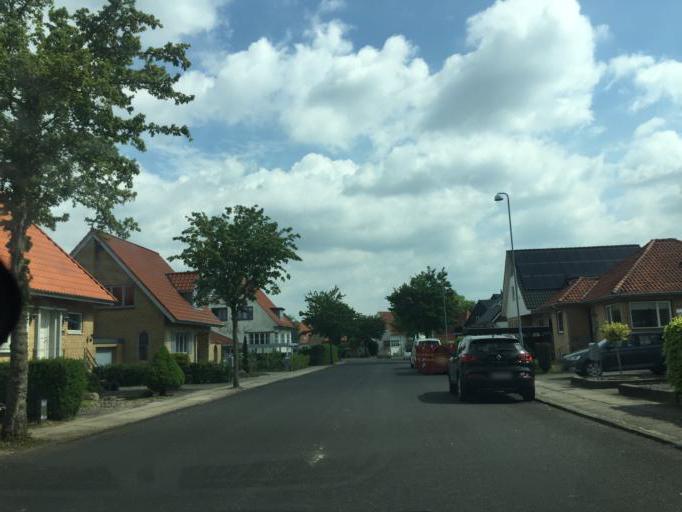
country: DK
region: South Denmark
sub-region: Odense Kommune
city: Odense
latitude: 55.3768
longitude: 10.3604
